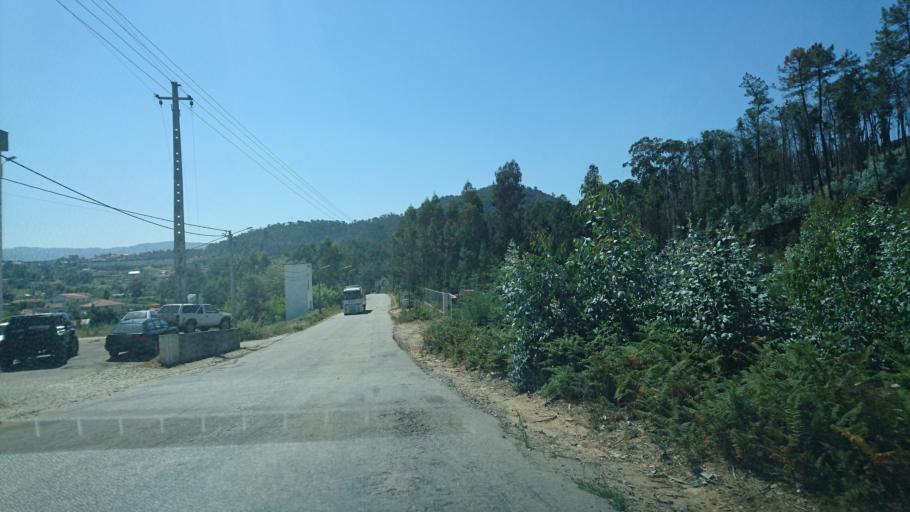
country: PT
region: Aveiro
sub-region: Oliveira de Azemeis
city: Vila Cha
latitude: 40.8826
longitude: -8.4289
